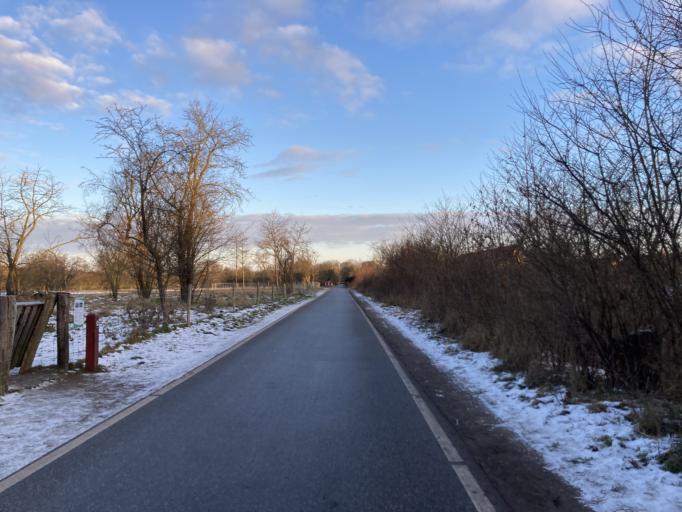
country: DK
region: Capital Region
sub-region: Gladsaxe Municipality
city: Buddinge
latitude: 55.7668
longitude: 12.4760
